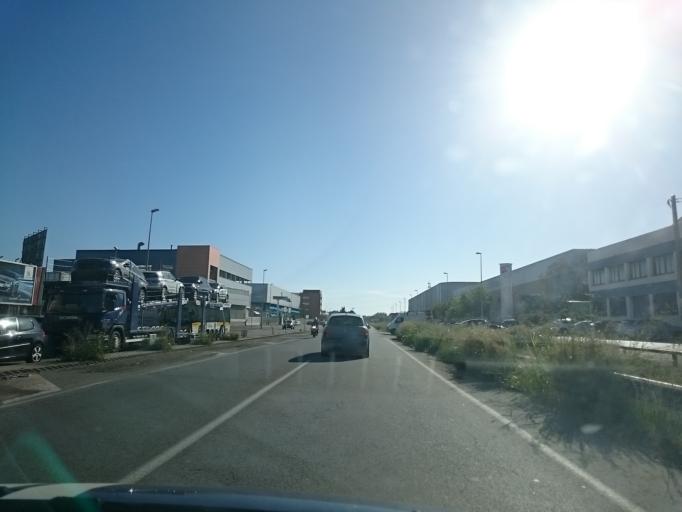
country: ES
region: Catalonia
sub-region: Provincia de Barcelona
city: Sant Boi de Llobregat
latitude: 41.3274
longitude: 2.0357
